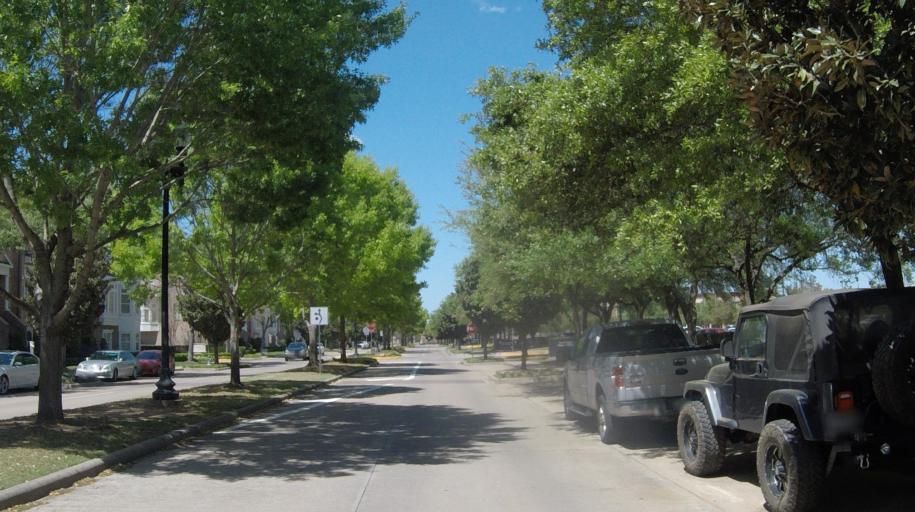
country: US
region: Texas
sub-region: Fort Bend County
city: Sugar Land
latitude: 29.6043
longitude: -95.6212
